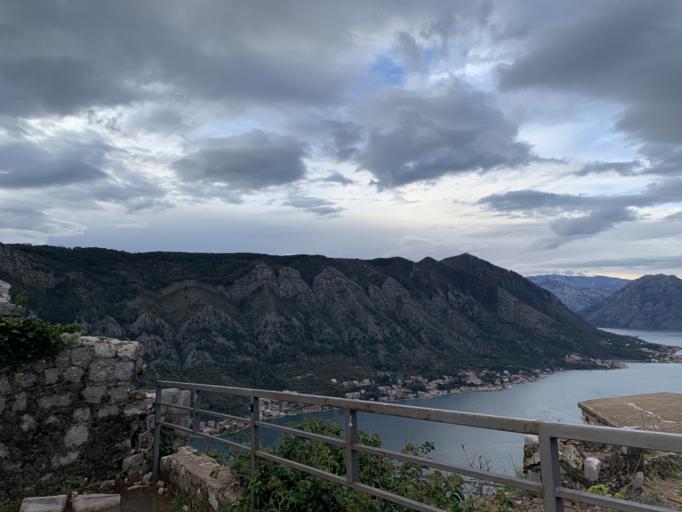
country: ME
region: Kotor
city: Kotor
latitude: 42.4218
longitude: 18.7751
